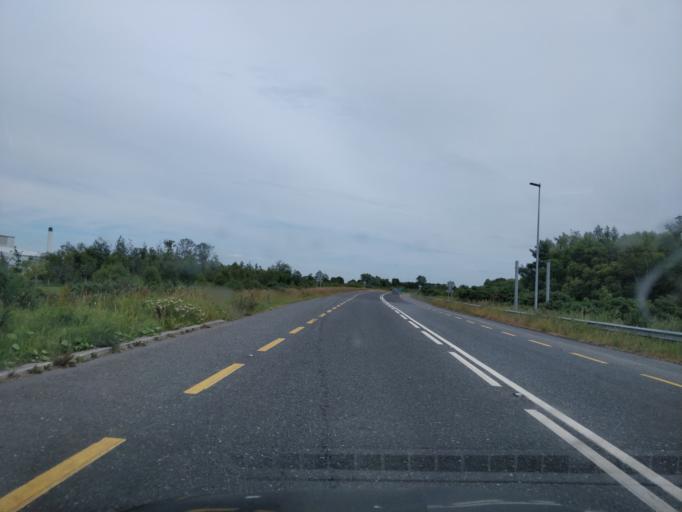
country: IE
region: Leinster
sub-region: Uibh Fhaili
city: Tullamore
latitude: 53.2521
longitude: -7.5015
